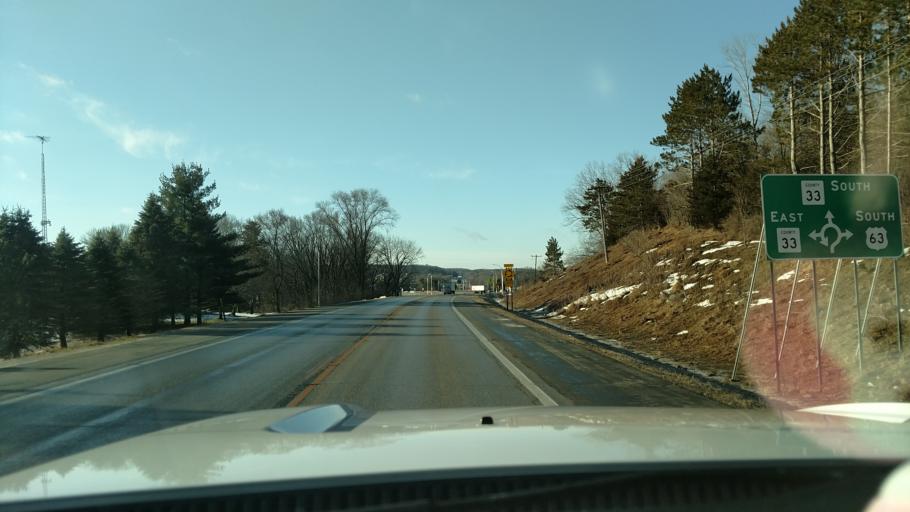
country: US
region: Minnesota
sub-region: Olmsted County
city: Rochester
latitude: 44.1115
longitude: -92.4290
